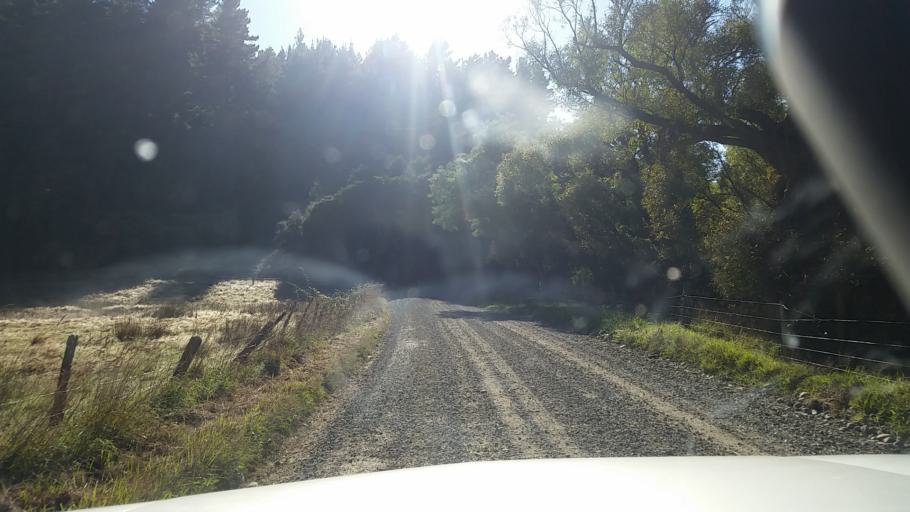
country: NZ
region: Marlborough
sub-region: Marlborough District
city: Blenheim
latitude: -41.4471
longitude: 173.8792
